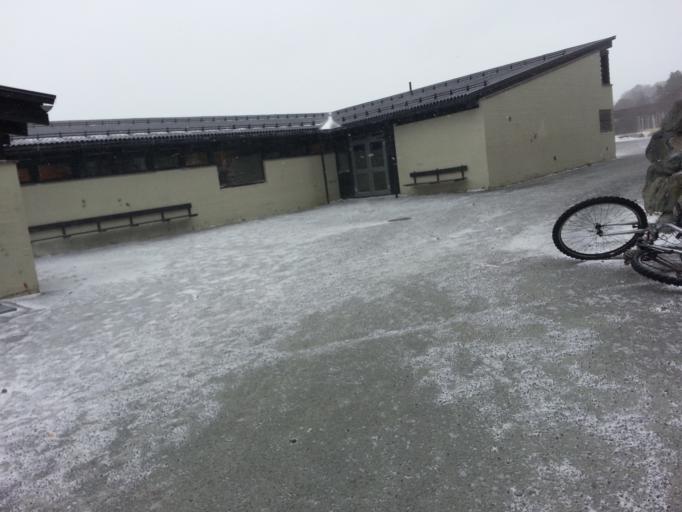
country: NO
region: Sor-Trondelag
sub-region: Oppdal
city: Oppdal
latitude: 62.5962
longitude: 9.6855
